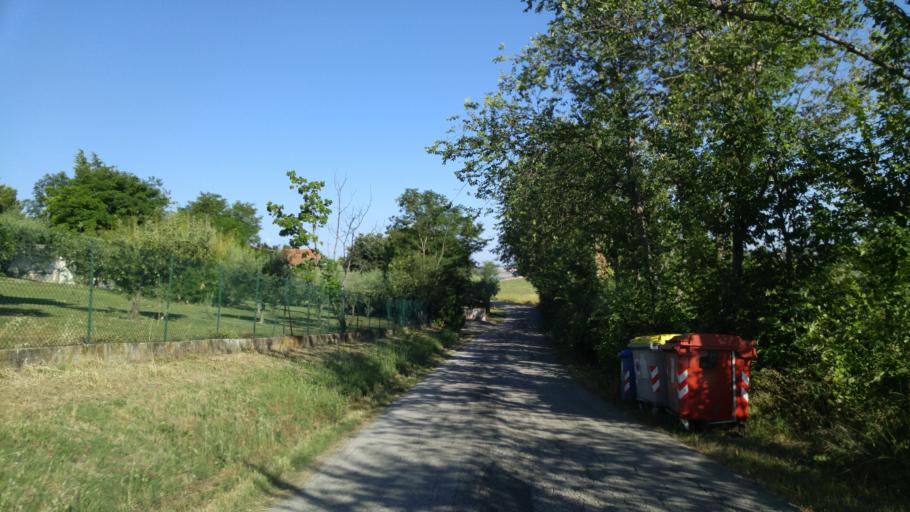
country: IT
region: The Marches
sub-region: Provincia di Pesaro e Urbino
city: Mombaroccio
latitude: 43.7971
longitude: 12.8830
